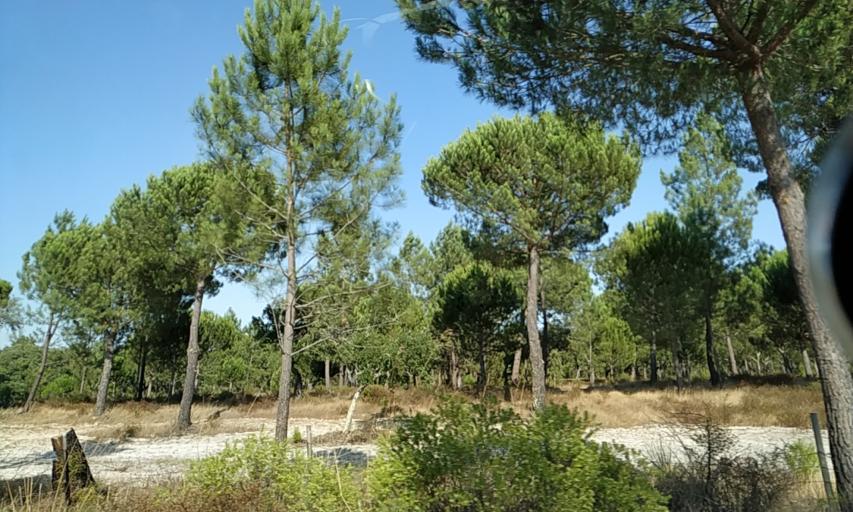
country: PT
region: Santarem
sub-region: Coruche
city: Coruche
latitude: 38.9078
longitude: -8.5269
